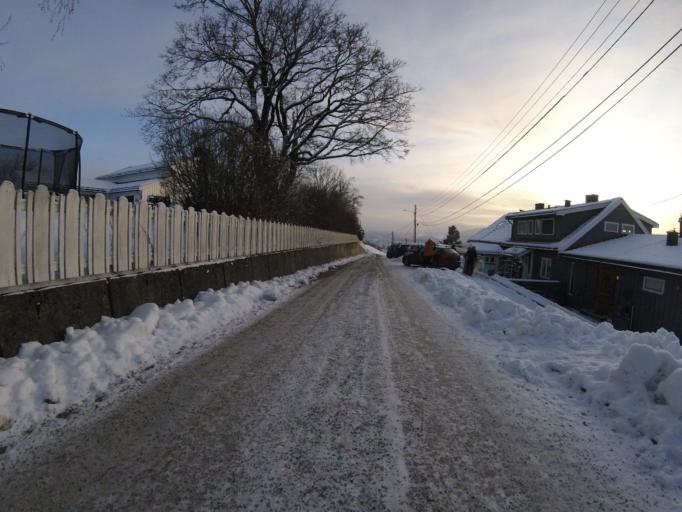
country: NO
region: Akershus
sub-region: Skedsmo
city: Lillestrom
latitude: 59.9674
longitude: 11.0609
